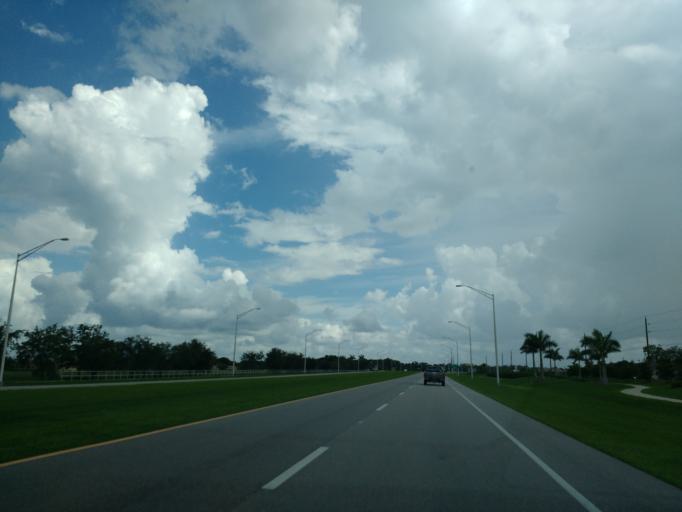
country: US
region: Florida
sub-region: Lee County
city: Burnt Store Marina
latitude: 26.7912
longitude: -82.0379
